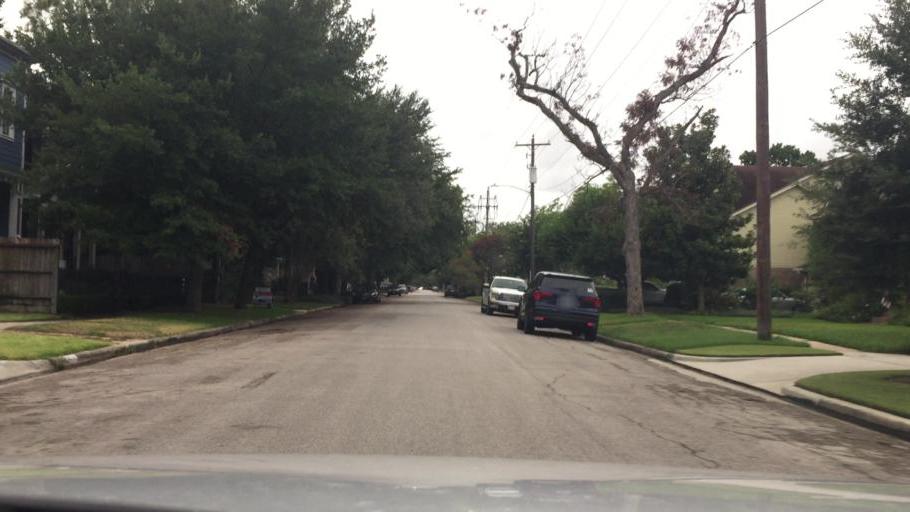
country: US
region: Texas
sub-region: Harris County
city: Houston
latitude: 29.7926
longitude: -95.3905
